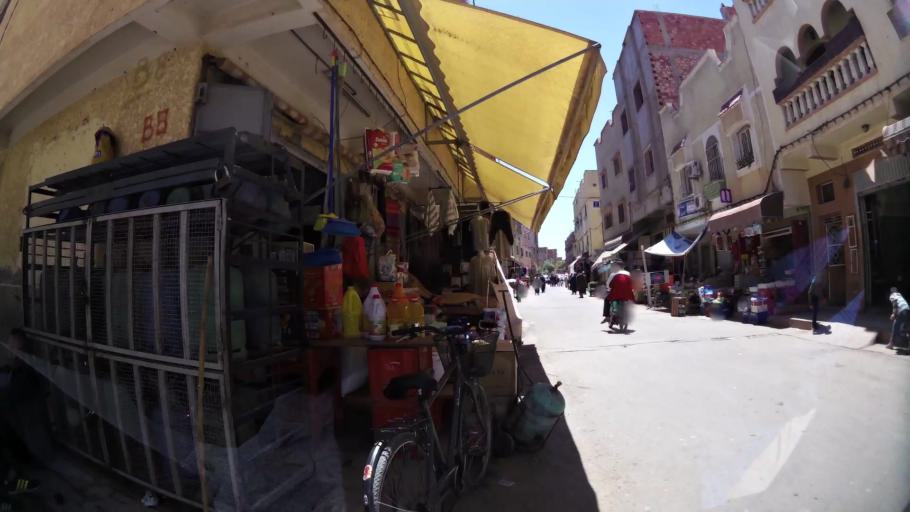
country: MA
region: Oriental
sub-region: Oujda-Angad
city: Oujda
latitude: 34.6609
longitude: -1.9226
